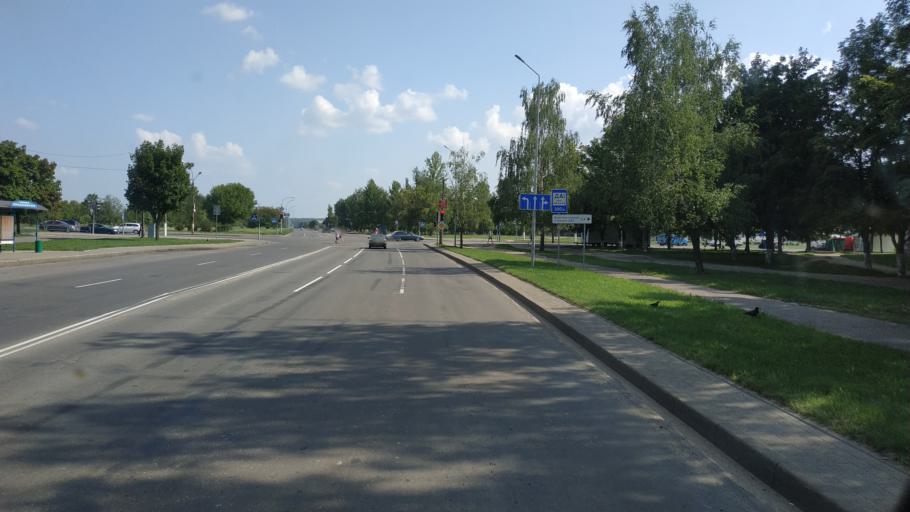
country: BY
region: Mogilev
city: Buynichy
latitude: 53.8670
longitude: 30.3147
